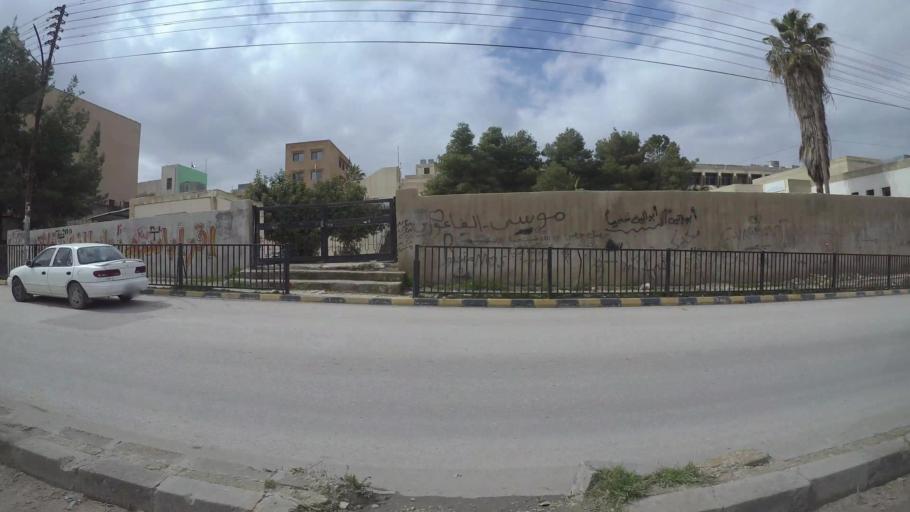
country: JO
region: Amman
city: Al Jubayhah
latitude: 32.0508
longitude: 35.8331
